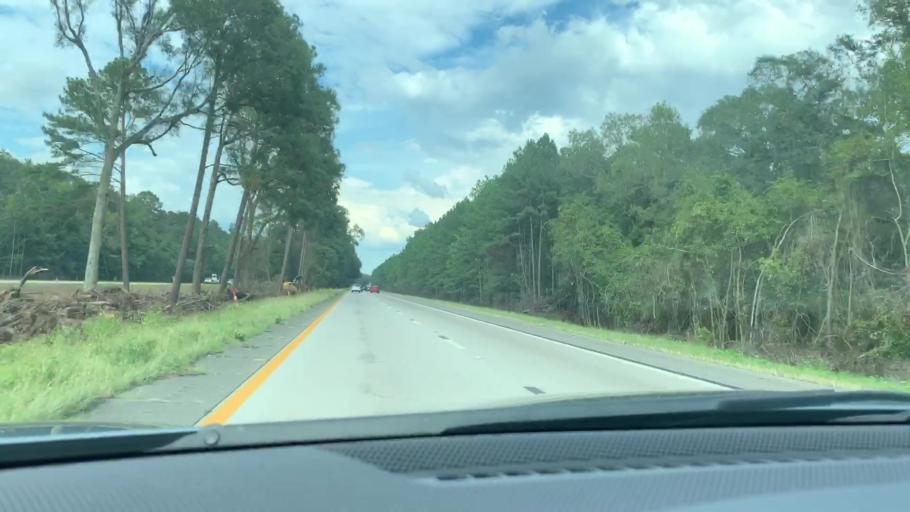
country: US
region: South Carolina
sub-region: Jasper County
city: Ridgeland
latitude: 32.4072
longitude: -81.0156
